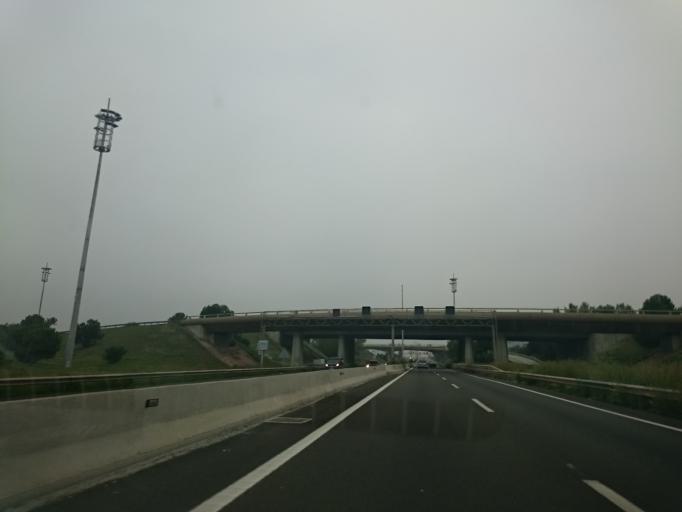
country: ES
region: Catalonia
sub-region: Provincia de Barcelona
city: El Prat de Llobregat
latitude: 41.3204
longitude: 2.0737
